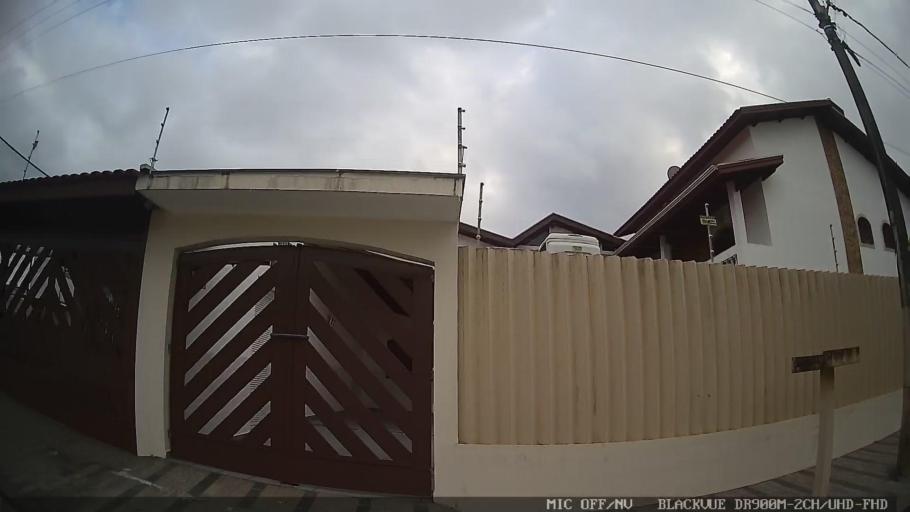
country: BR
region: Sao Paulo
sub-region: Itanhaem
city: Itanhaem
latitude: -24.1950
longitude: -46.8154
